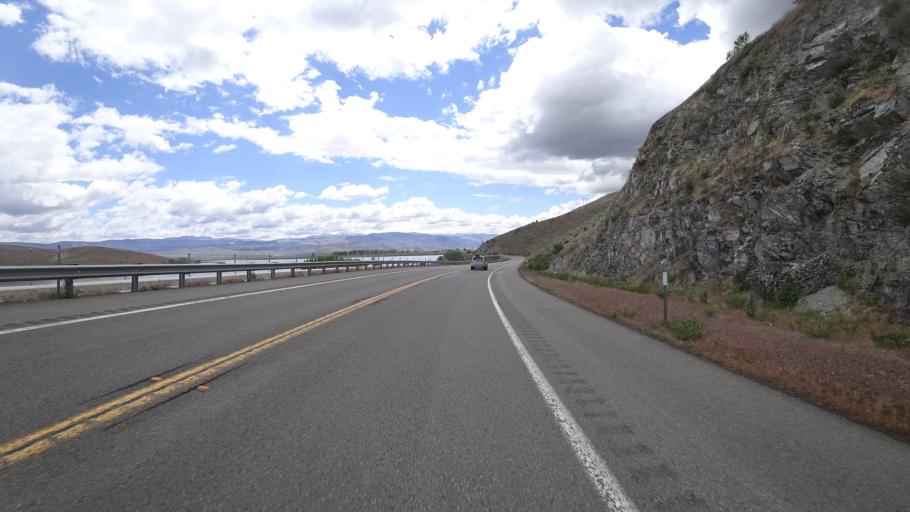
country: US
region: Nevada
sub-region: Lyon County
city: Smith Valley
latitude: 38.6667
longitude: -119.5440
